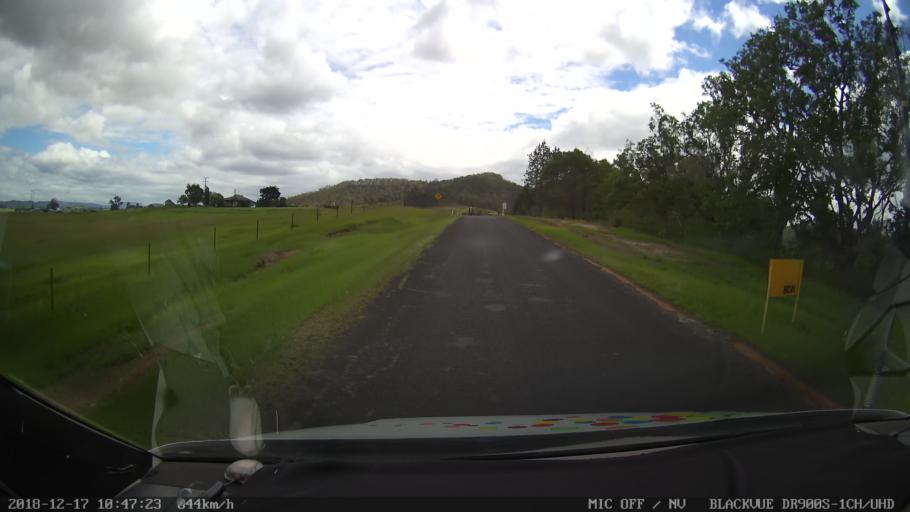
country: AU
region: New South Wales
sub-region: Clarence Valley
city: Gordon
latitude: -28.8809
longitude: 152.5706
